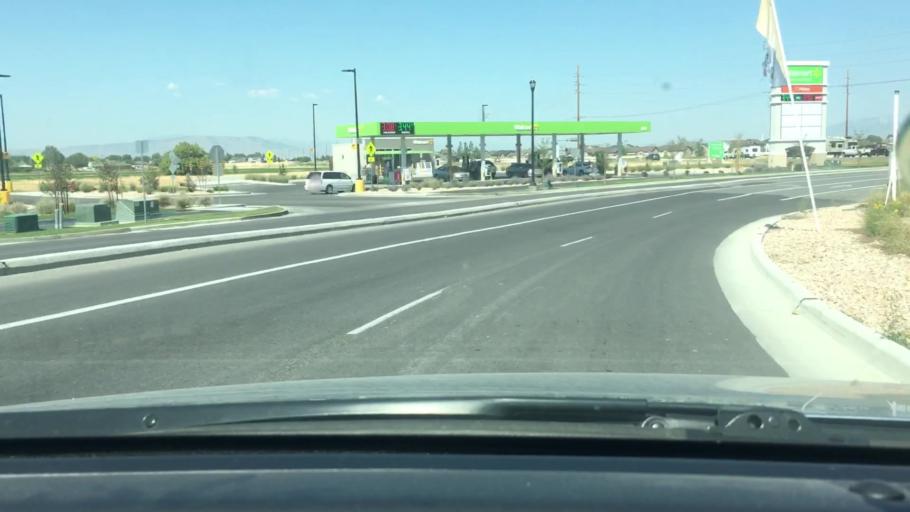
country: US
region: Utah
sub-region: Utah County
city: Spanish Fork
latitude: 40.0983
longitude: -111.6124
